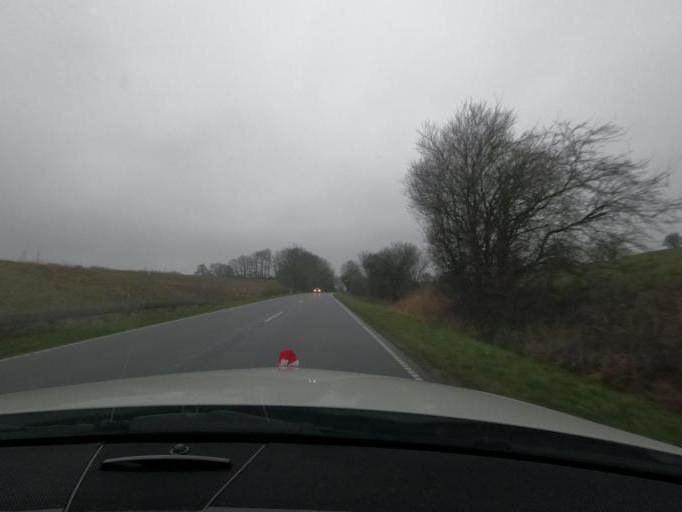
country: DK
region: South Denmark
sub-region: Haderslev Kommune
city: Vojens
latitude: 55.1795
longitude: 9.3978
